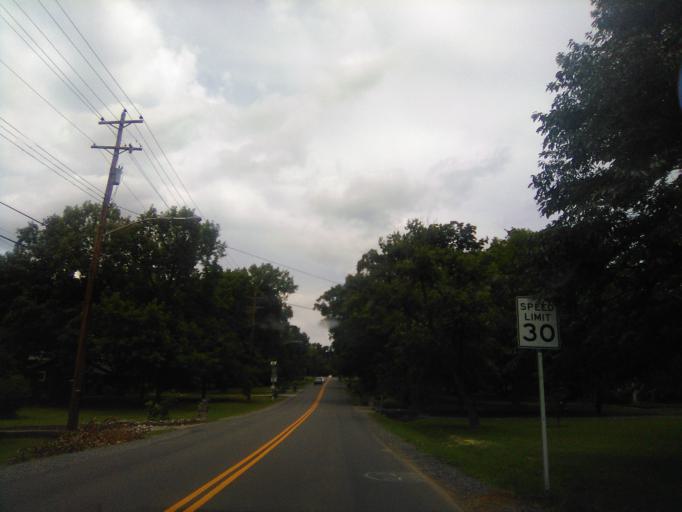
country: US
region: Tennessee
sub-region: Davidson County
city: Belle Meade
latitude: 36.1226
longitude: -86.8865
